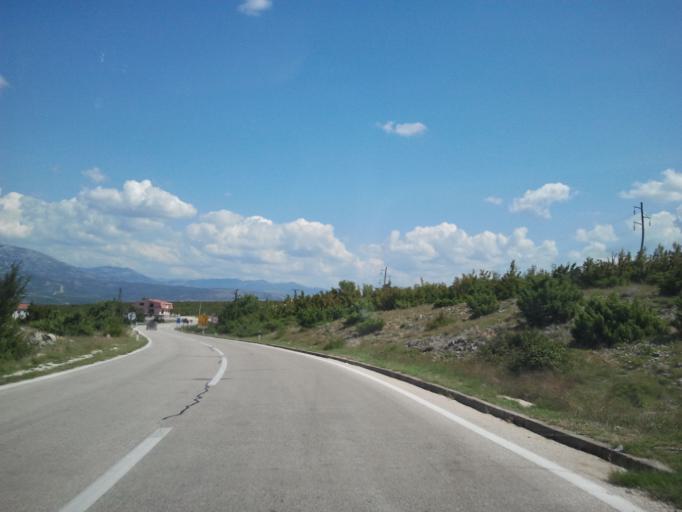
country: HR
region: Zadarska
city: Obrovac
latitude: 44.1941
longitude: 15.6772
